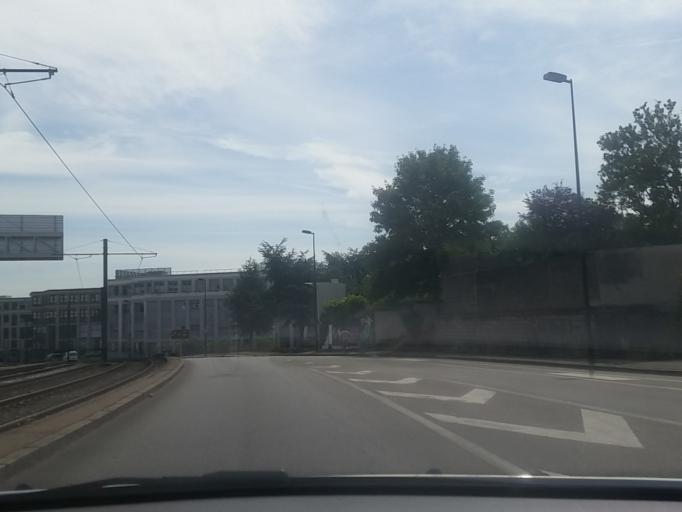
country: FR
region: Pays de la Loire
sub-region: Departement de la Loire-Atlantique
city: Nantes
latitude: 47.2066
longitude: -1.5776
